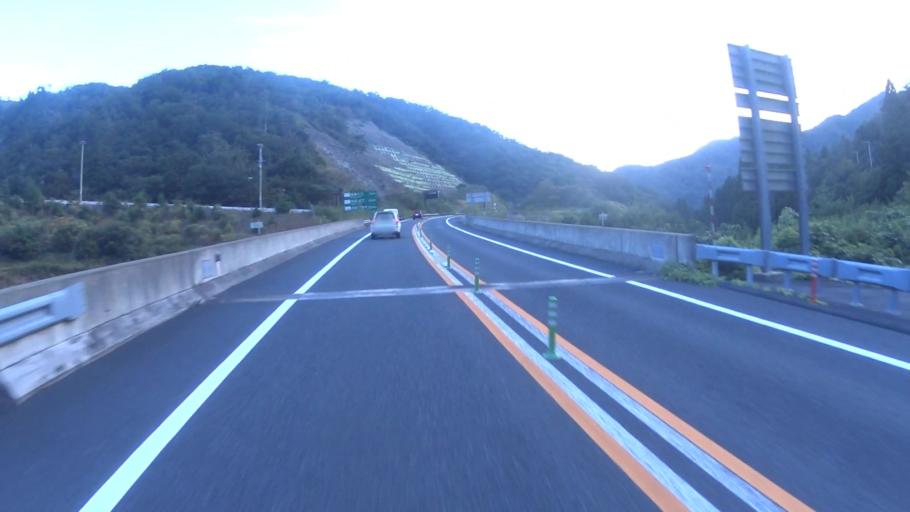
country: JP
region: Kyoto
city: Miyazu
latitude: 35.4730
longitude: 135.1757
